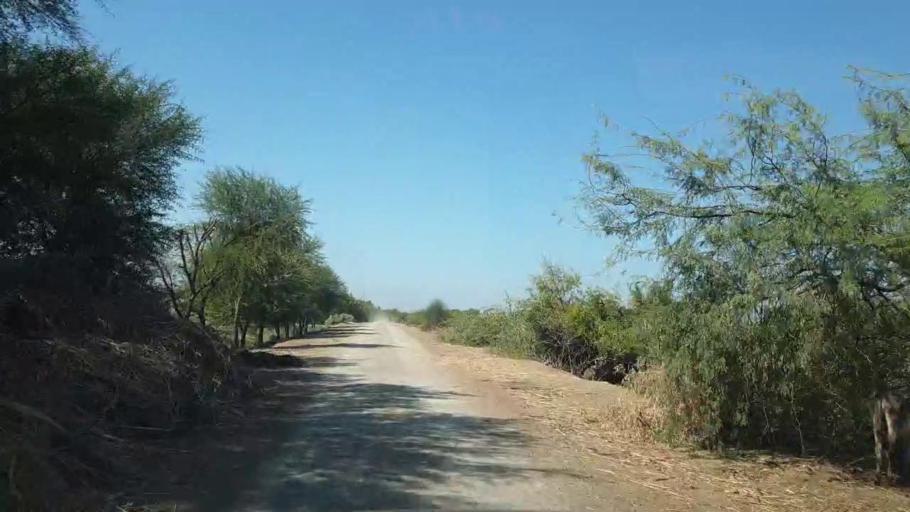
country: PK
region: Sindh
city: Mirpur Khas
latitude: 25.6125
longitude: 69.1406
